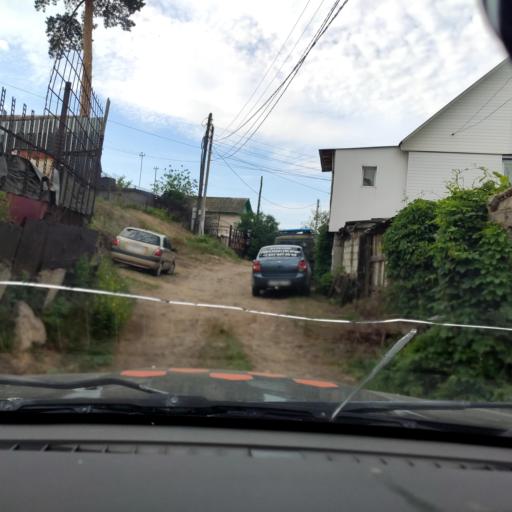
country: RU
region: Samara
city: Zhigulevsk
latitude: 53.4682
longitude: 49.5729
